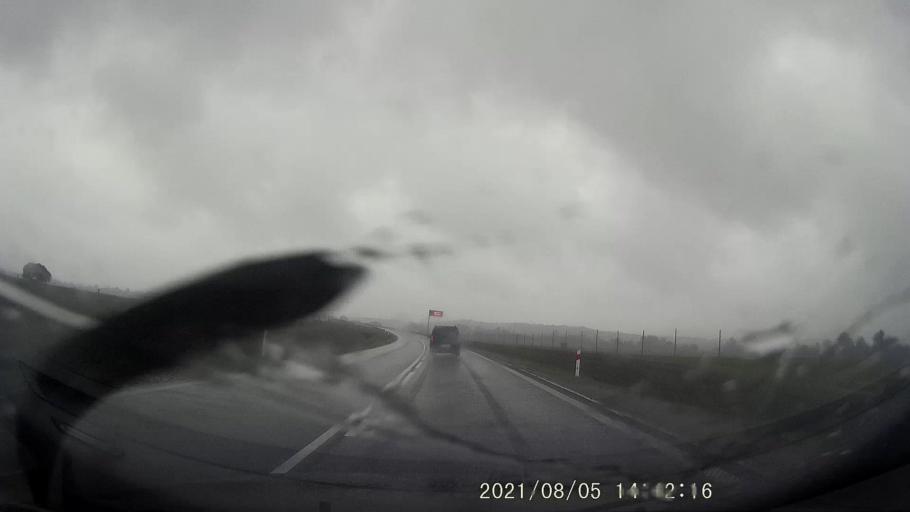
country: PL
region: Opole Voivodeship
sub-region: Powiat nyski
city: Nysa
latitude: 50.4731
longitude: 17.4055
